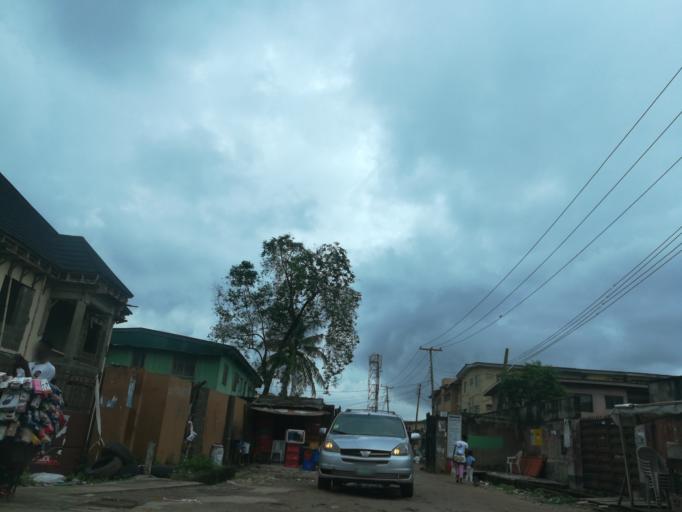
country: NG
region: Lagos
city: Agege
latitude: 6.6051
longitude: 3.3106
